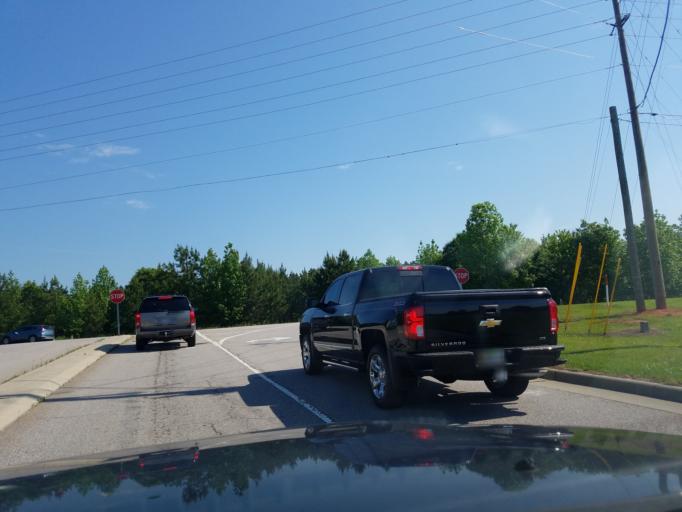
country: US
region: North Carolina
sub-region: Vance County
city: Henderson
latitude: 36.3383
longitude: -78.4452
